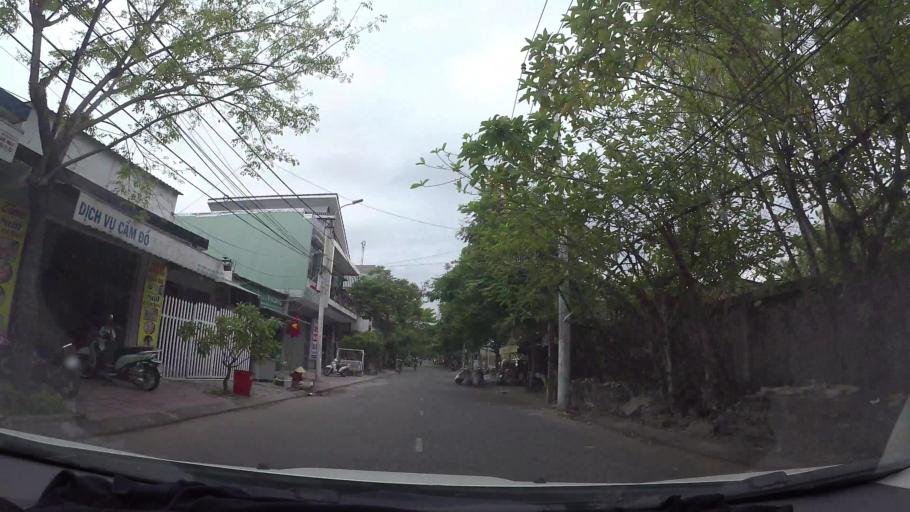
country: VN
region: Da Nang
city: Lien Chieu
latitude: 16.1230
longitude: 108.1199
